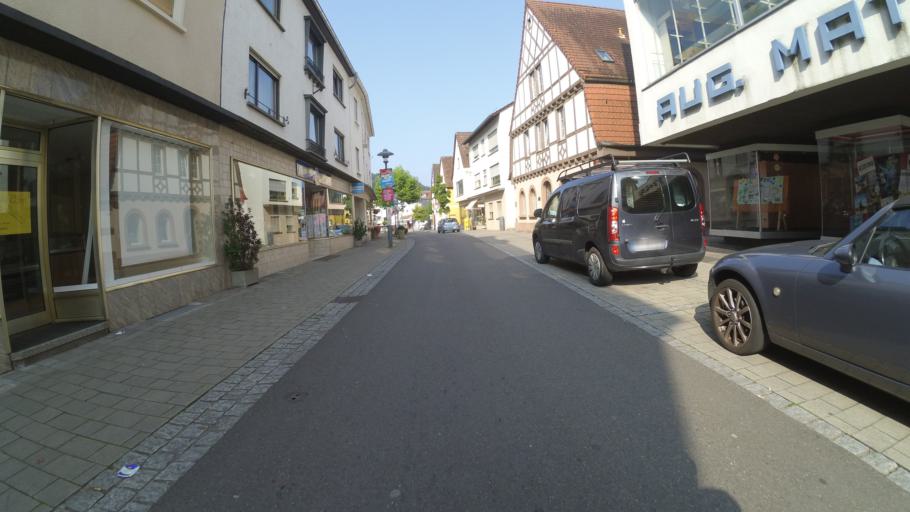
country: DE
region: Rheinland-Pfalz
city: Rodalben
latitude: 49.2404
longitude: 7.6326
